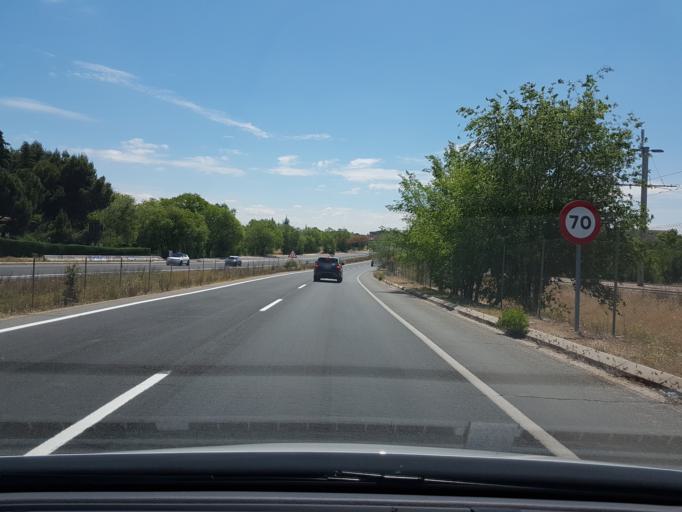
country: ES
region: Madrid
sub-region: Provincia de Madrid
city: Pozuelo de Alarcon
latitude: 40.4244
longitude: -3.8061
